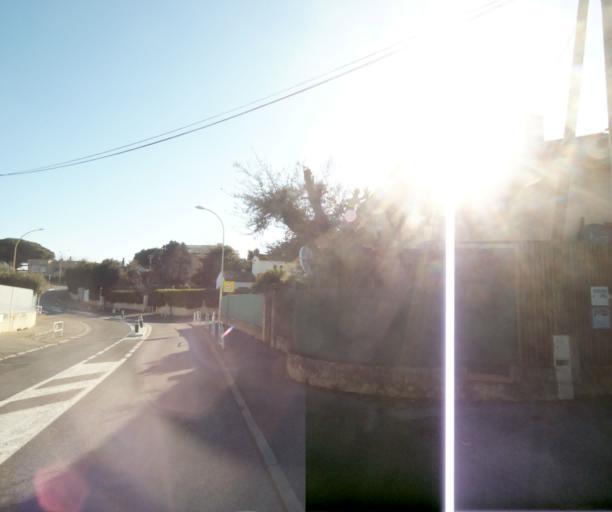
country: FR
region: Provence-Alpes-Cote d'Azur
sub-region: Departement des Alpes-Maritimes
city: Biot
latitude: 43.6040
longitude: 7.1212
